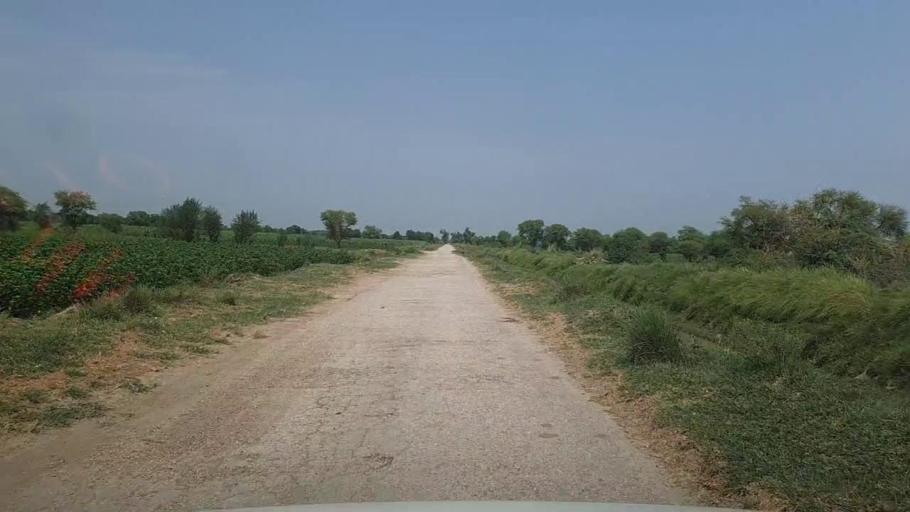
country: PK
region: Sindh
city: Karaundi
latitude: 26.8853
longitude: 68.3342
